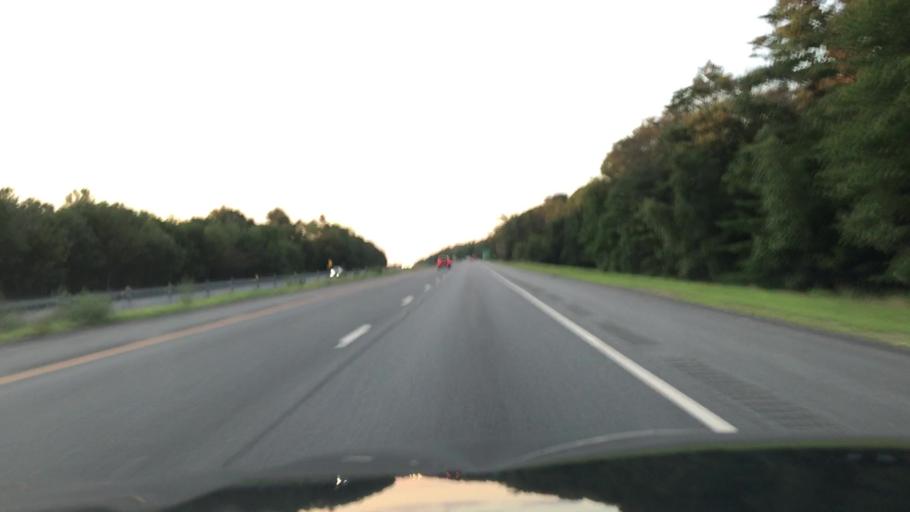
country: US
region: Rhode Island
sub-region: Kent County
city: West Greenwich
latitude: 41.5792
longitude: -71.6604
